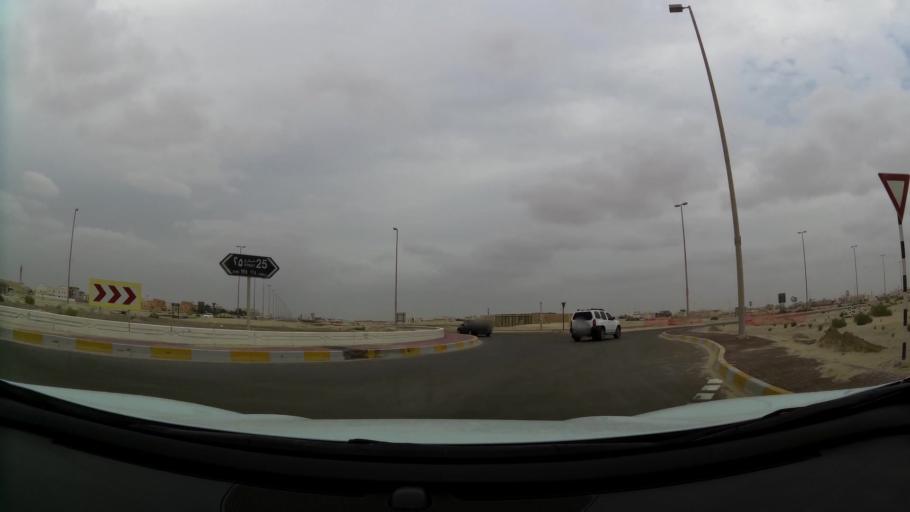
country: AE
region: Abu Dhabi
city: Abu Dhabi
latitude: 24.3624
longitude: 54.6331
